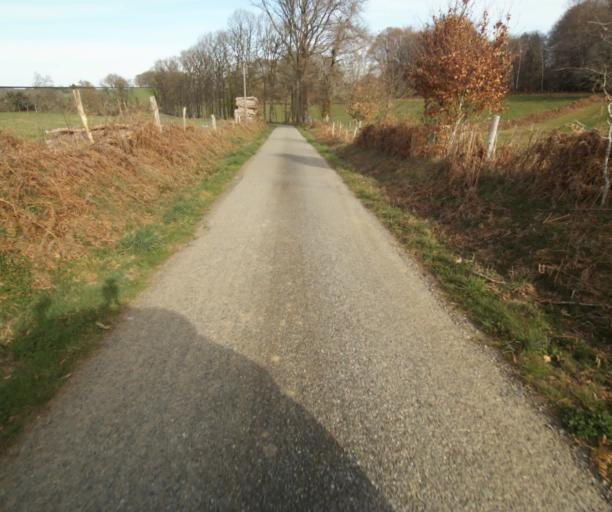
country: FR
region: Limousin
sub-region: Departement de la Correze
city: Chamboulive
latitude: 45.4270
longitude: 1.7516
